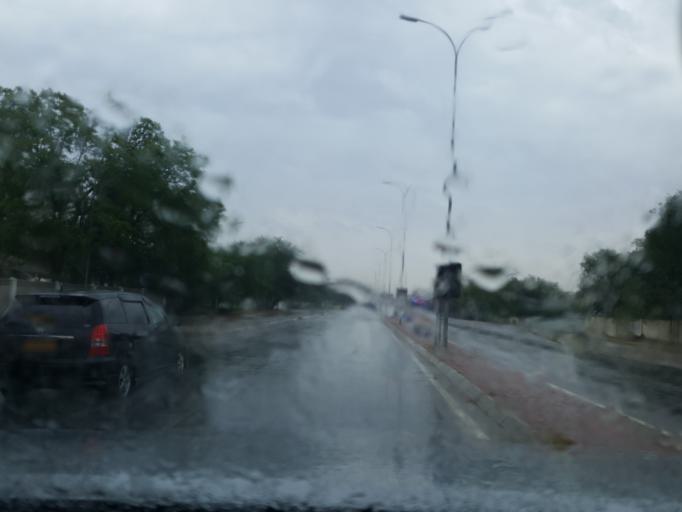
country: BW
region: South East
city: Gaborone
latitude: -24.6435
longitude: 25.9240
